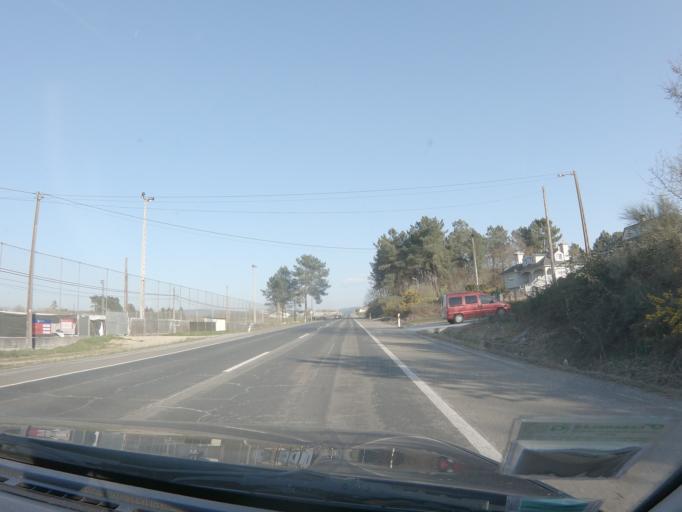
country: ES
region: Galicia
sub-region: Provincia de Lugo
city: Corgo
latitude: 42.9360
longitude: -7.4085
